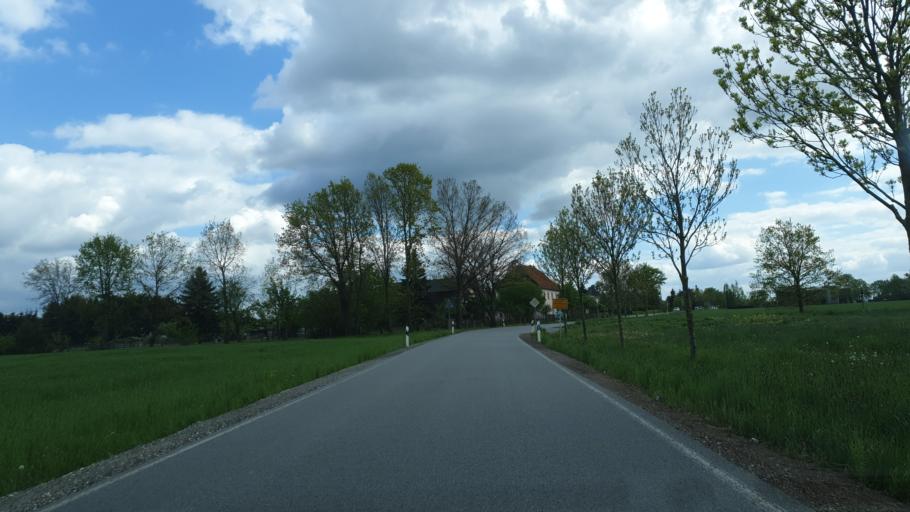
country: DE
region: Saxony
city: Niederdorf
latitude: 50.7648
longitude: 12.7758
